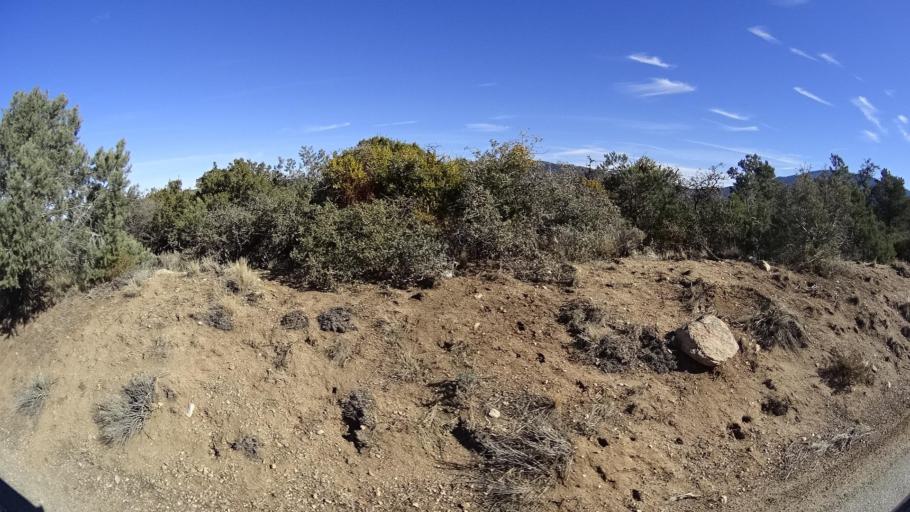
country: US
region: California
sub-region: Kern County
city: Pine Mountain Club
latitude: 34.8716
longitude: -119.2966
